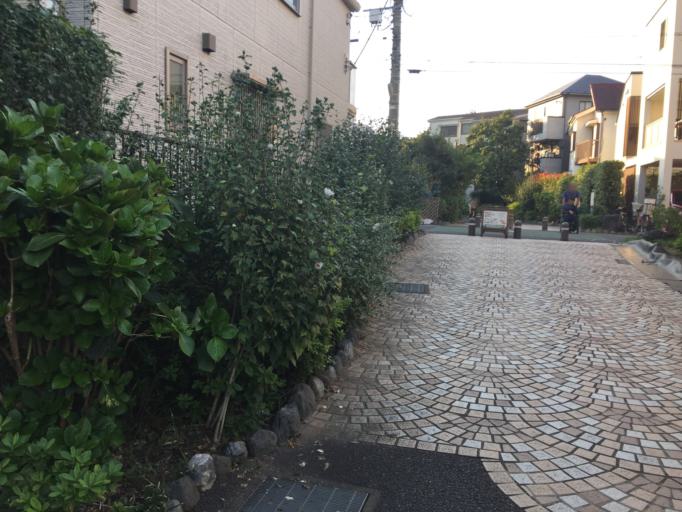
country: JP
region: Tokyo
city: Tokyo
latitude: 35.6472
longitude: 139.6630
